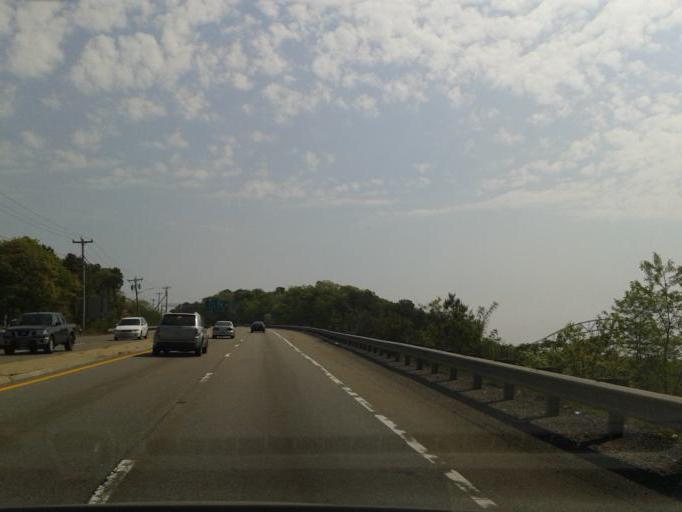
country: US
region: Massachusetts
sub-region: Barnstable County
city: Sagamore
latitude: 41.7753
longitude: -70.5572
